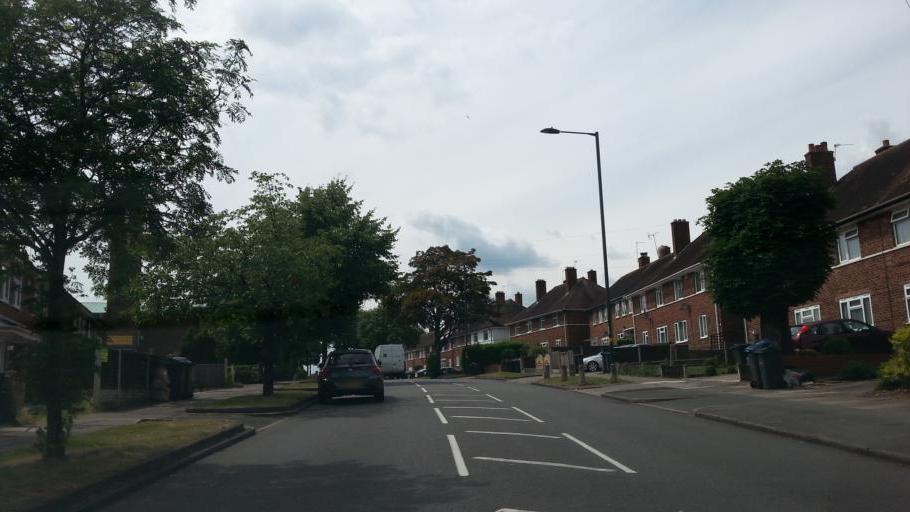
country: GB
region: England
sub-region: City and Borough of Birmingham
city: Acocks Green
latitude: 52.4699
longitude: -1.7849
